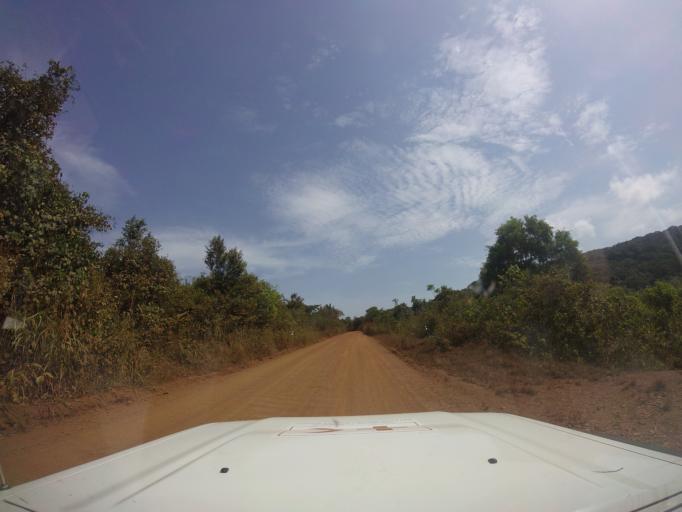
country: LR
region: Grand Cape Mount
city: Robertsport
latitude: 6.7321
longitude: -11.3403
